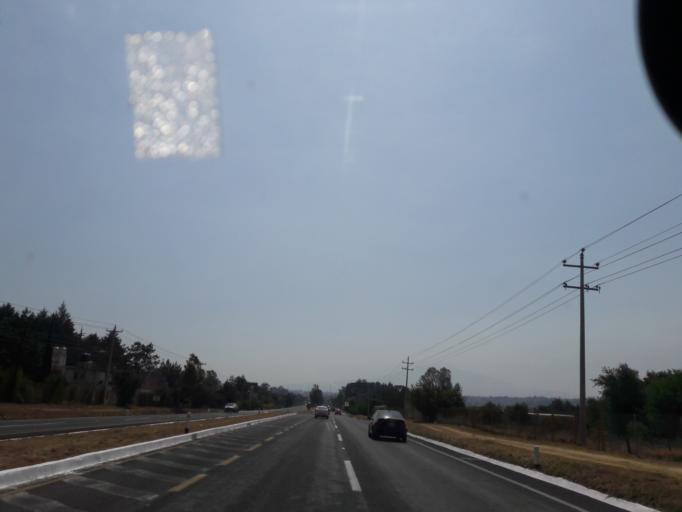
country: MX
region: Tlaxcala
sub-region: Panotla
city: Fraccionamiento la Virgen
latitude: 19.3221
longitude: -98.2720
